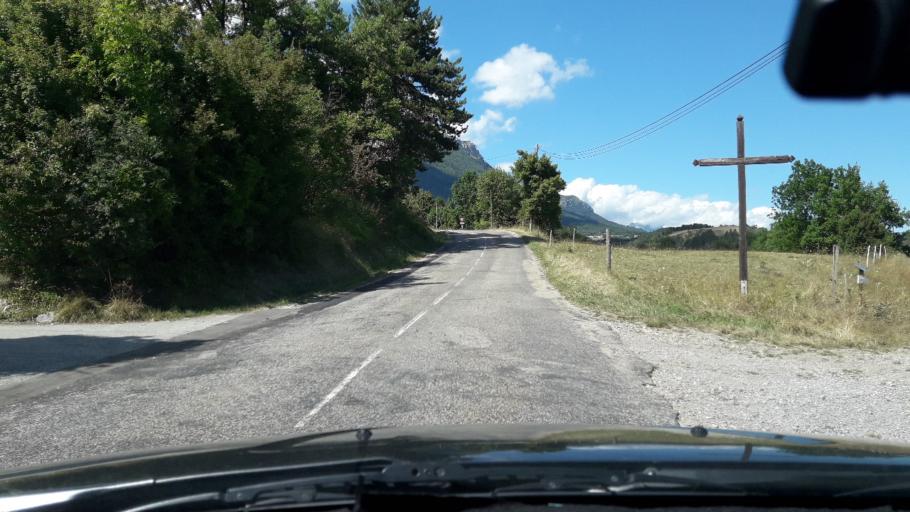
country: FR
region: Rhone-Alpes
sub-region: Departement de l'Isere
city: Mens
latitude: 44.8495
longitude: 5.6225
